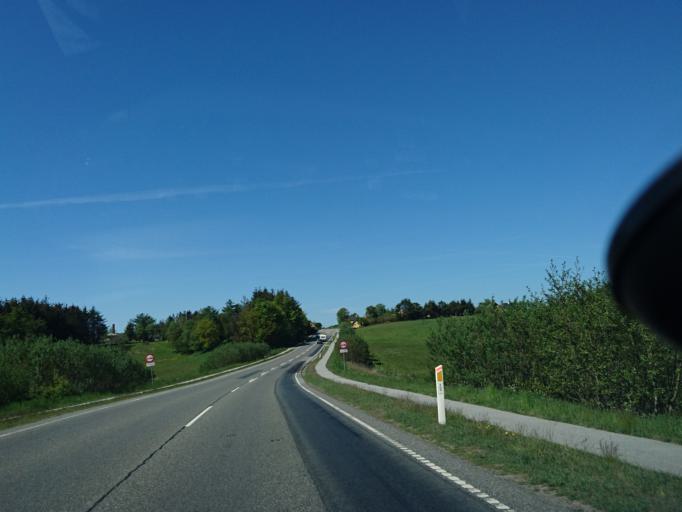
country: DK
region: North Denmark
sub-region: Hjorring Kommune
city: Sindal
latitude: 57.4556
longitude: 10.1329
